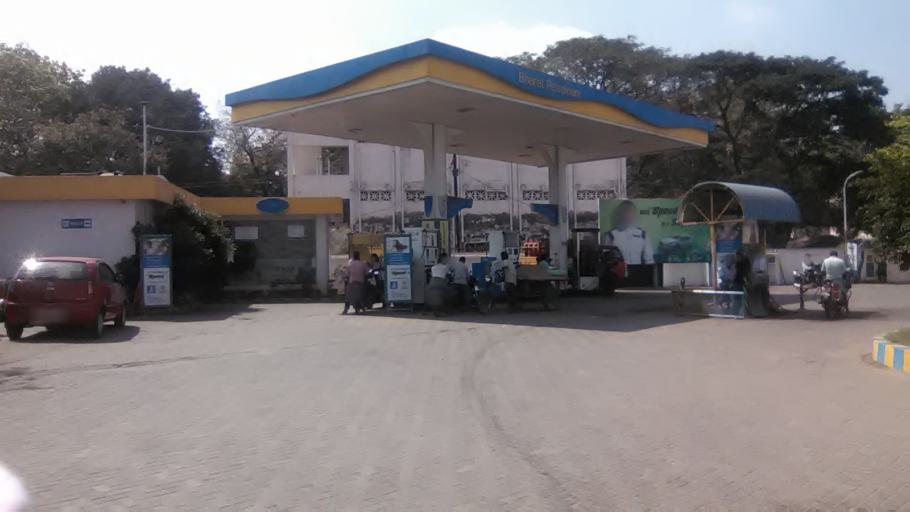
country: IN
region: Tamil Nadu
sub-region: Tiruchchirappalli
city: Tiruchirappalli
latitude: 10.7879
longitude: 78.6953
